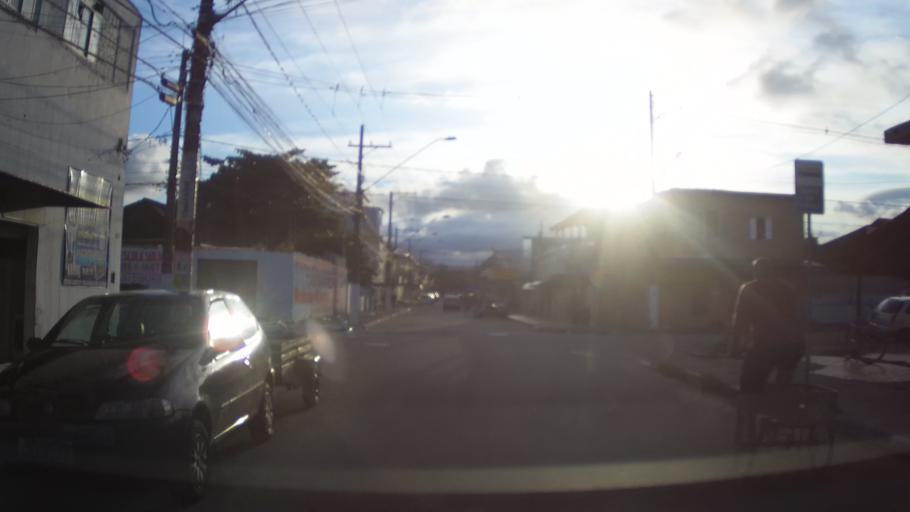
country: BR
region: Sao Paulo
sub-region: Sao Vicente
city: Sao Vicente
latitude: -23.9695
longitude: -46.3976
